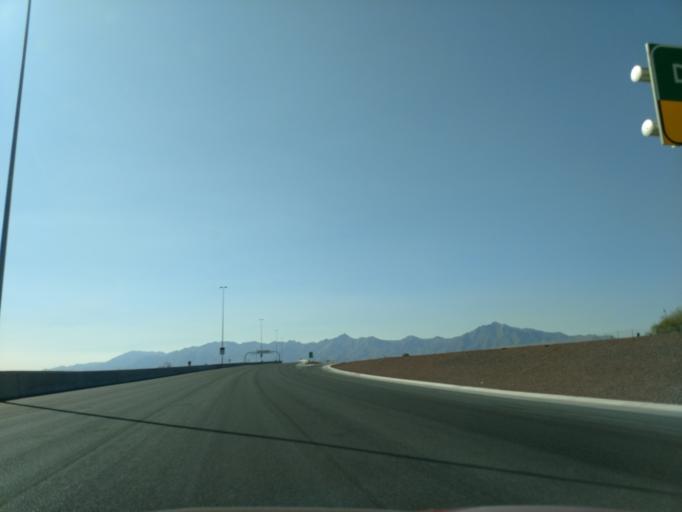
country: US
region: Arizona
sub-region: Maricopa County
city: Laveen
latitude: 33.3683
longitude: -112.1907
